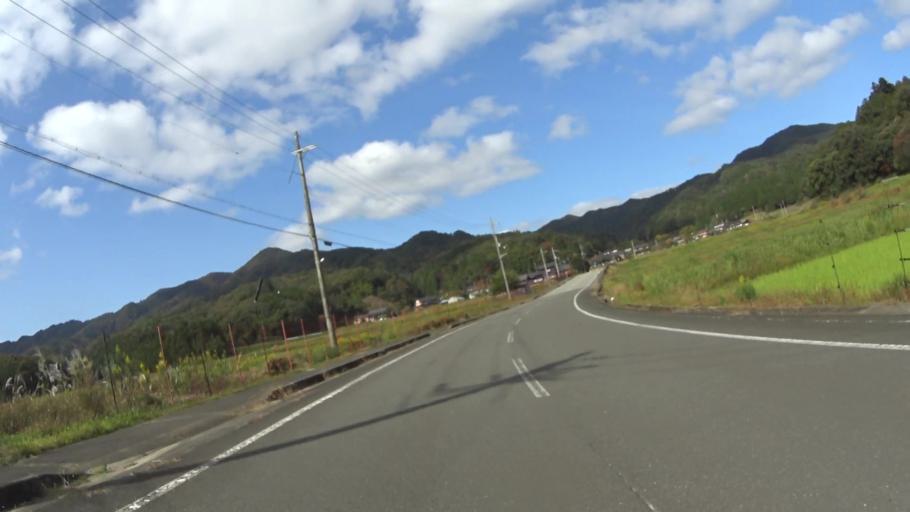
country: JP
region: Hyogo
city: Toyooka
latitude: 35.5043
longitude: 134.9923
